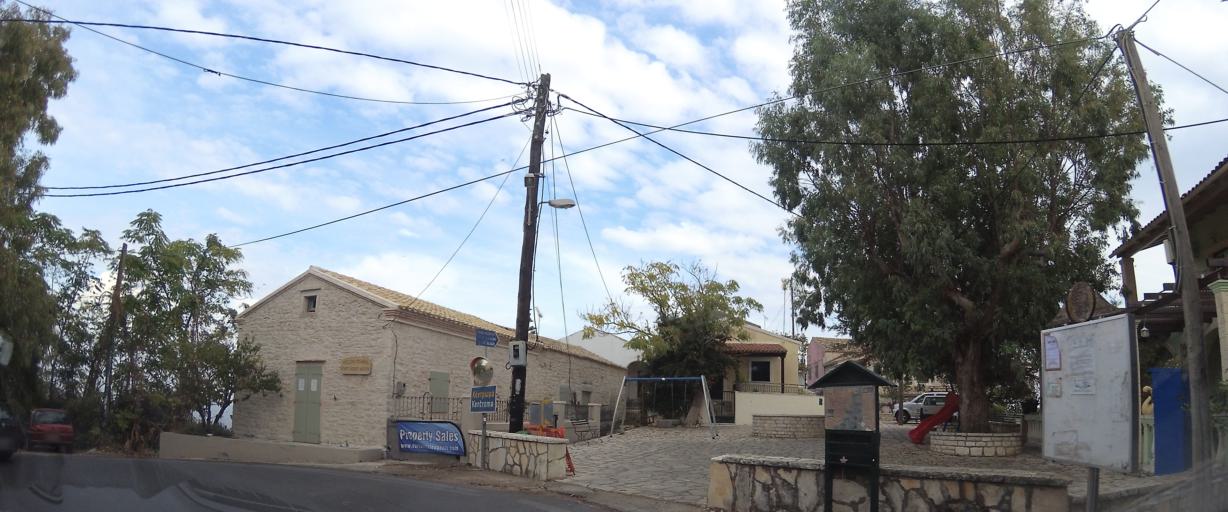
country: GR
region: Ionian Islands
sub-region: Nomos Kerkyras
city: Kerkyra
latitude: 39.7350
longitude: 19.9243
